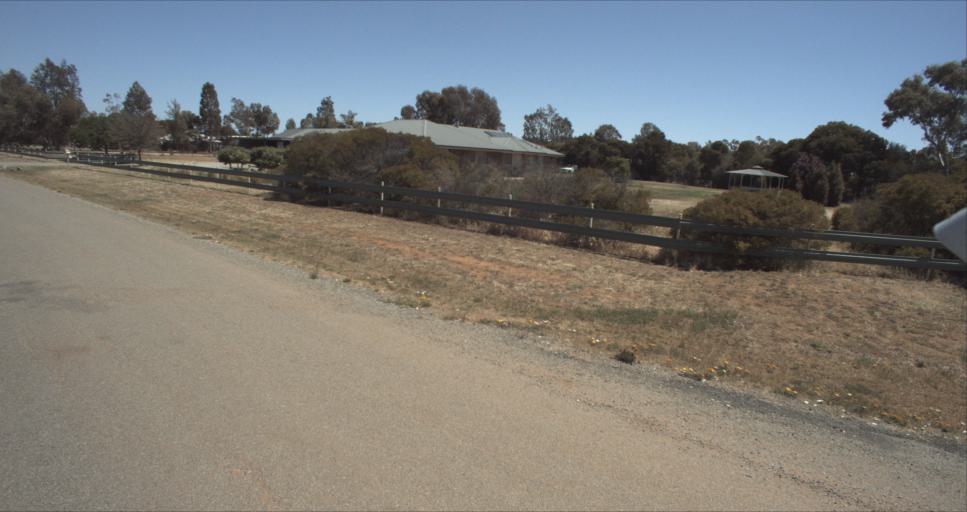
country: AU
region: New South Wales
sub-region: Leeton
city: Leeton
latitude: -34.5306
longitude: 146.3960
